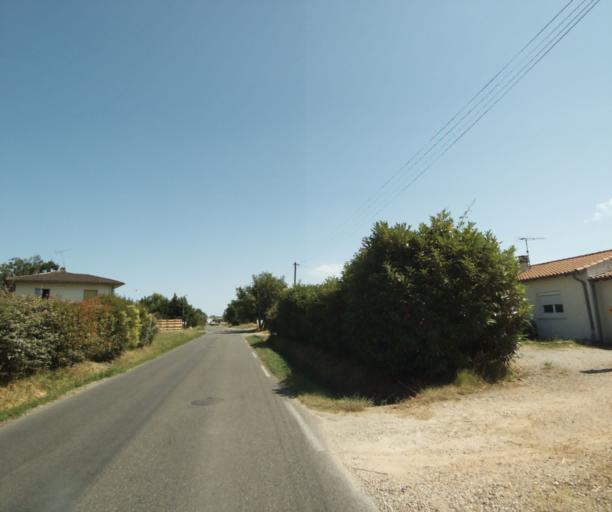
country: FR
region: Midi-Pyrenees
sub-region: Departement du Tarn-et-Garonne
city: Montauban
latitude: 44.0403
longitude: 1.3712
